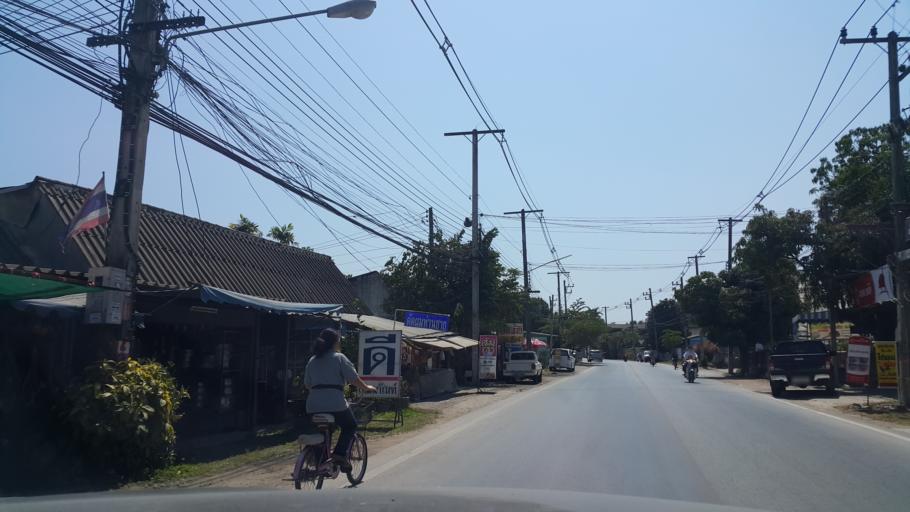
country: TH
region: Chiang Mai
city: San Sai
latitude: 18.8728
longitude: 99.0514
